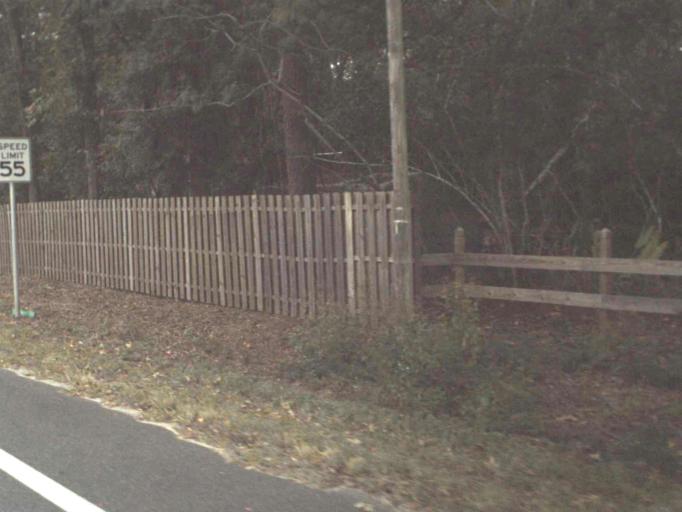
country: US
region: Florida
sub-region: Wakulla County
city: Crawfordville
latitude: 30.1122
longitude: -84.3822
